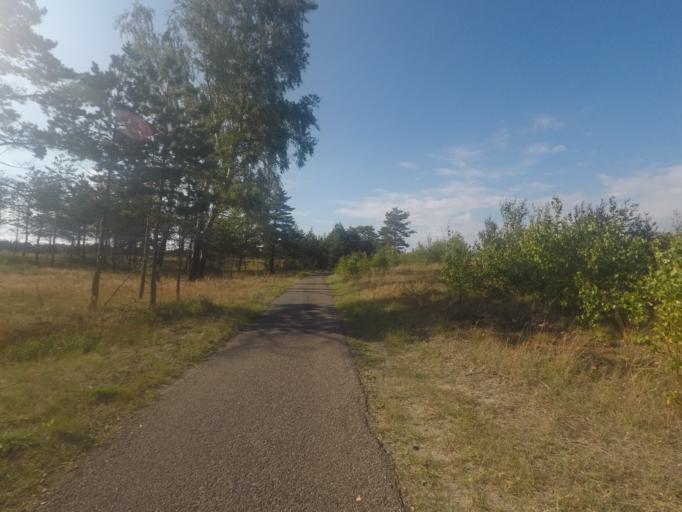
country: LT
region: Klaipedos apskritis
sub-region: Klaipeda
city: Klaipeda
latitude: 55.5942
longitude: 21.1154
